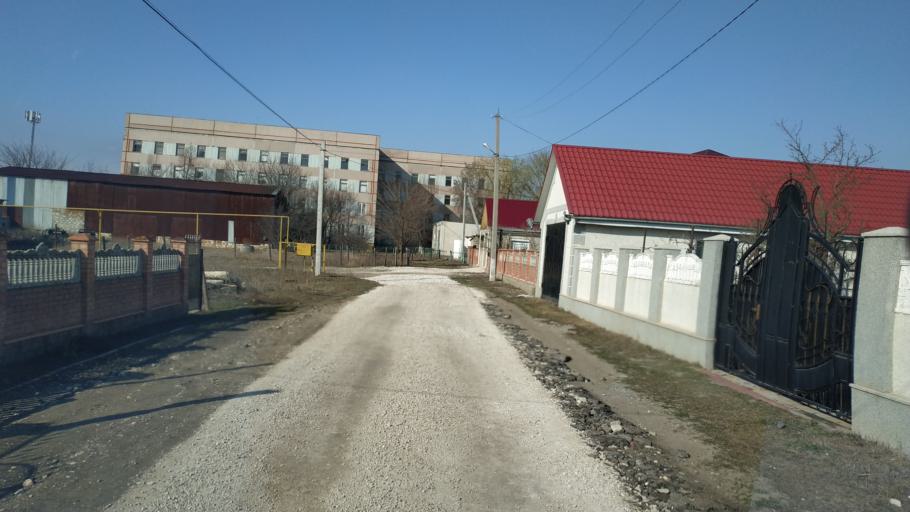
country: MD
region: Chisinau
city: Singera
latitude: 46.6851
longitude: 29.0597
